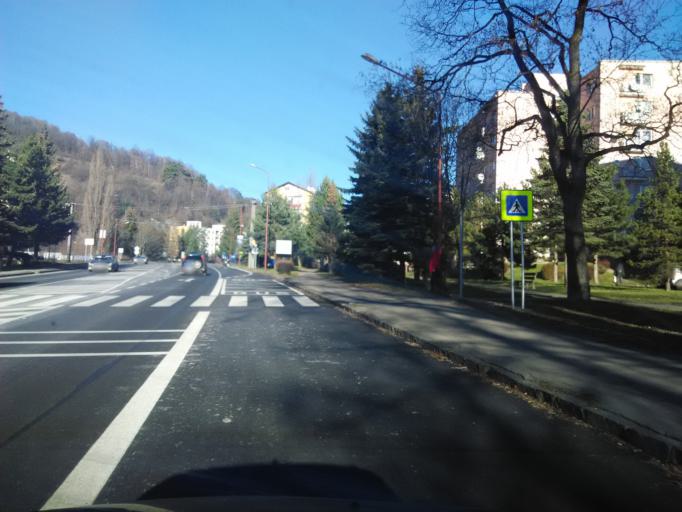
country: SK
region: Banskobystricky
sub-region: Okres Ziar nad Hronom
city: Kremnica
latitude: 48.6985
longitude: 18.9150
